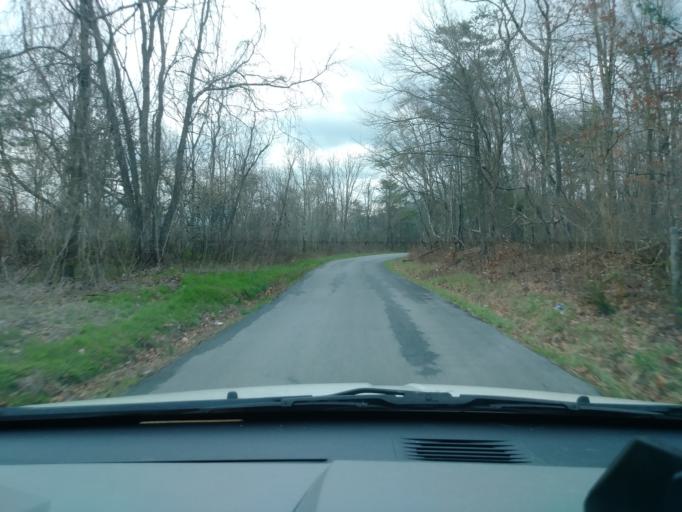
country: US
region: Tennessee
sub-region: Greene County
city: Tusculum
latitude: 36.0859
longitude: -82.7349
